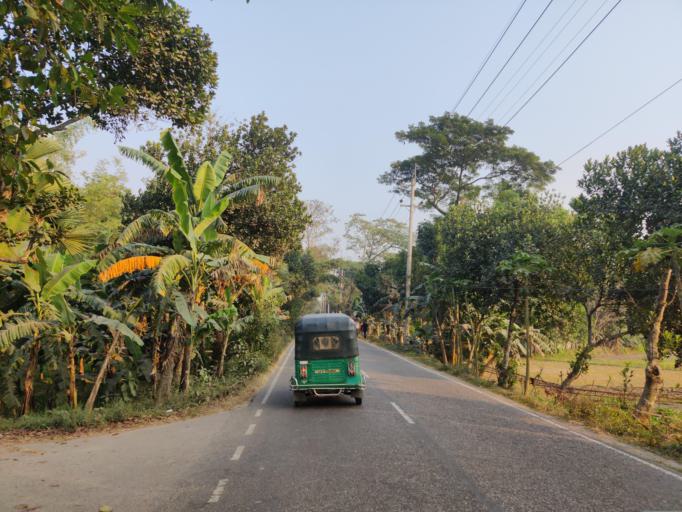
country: BD
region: Dhaka
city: Narsingdi
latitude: 24.0954
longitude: 90.7187
